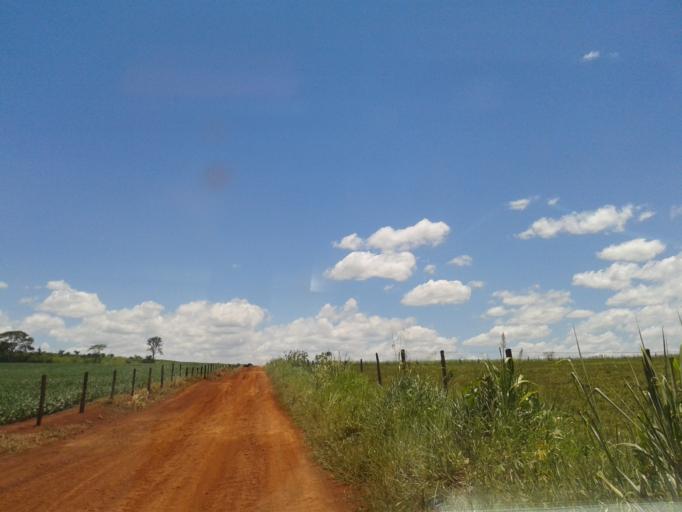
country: BR
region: Minas Gerais
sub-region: Centralina
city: Centralina
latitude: -18.6698
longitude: -49.2316
